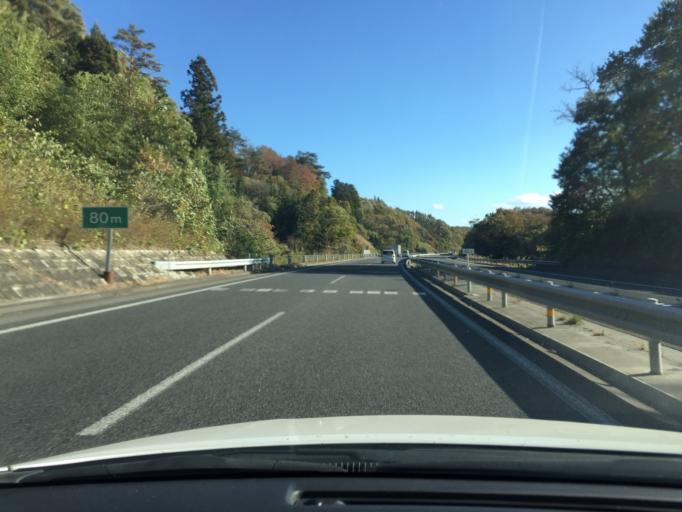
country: JP
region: Fukushima
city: Funehikimachi-funehiki
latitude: 37.3336
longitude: 140.6151
